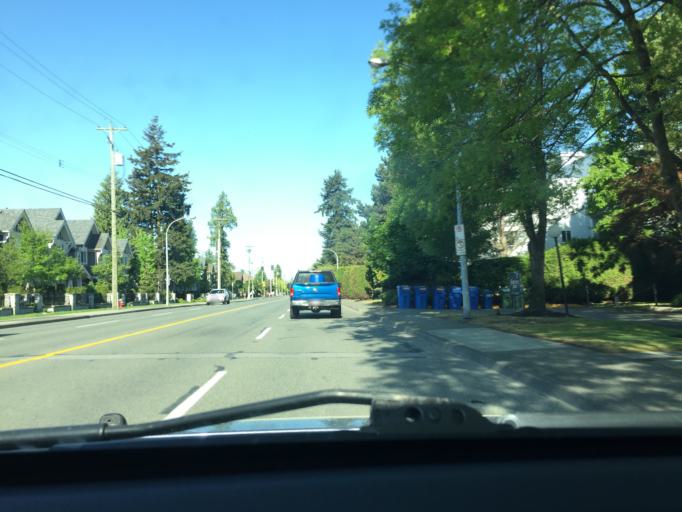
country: CA
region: British Columbia
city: Richmond
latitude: 49.1557
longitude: -123.1416
